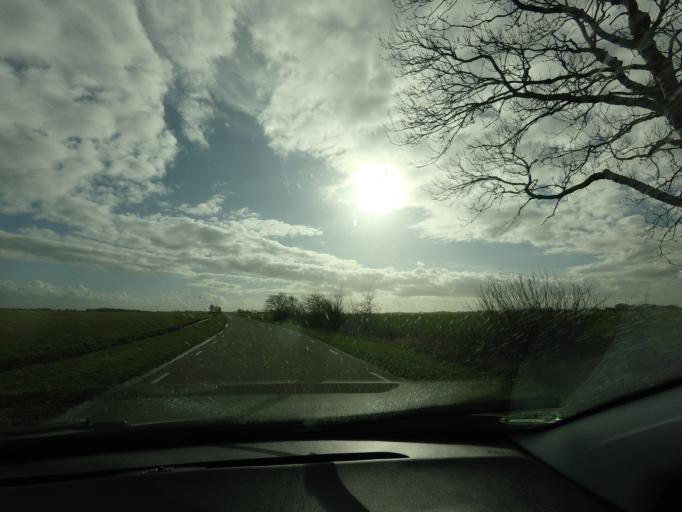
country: NL
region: Friesland
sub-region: Gemeente Boarnsterhim
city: Jirnsum
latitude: 53.0635
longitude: 5.7411
